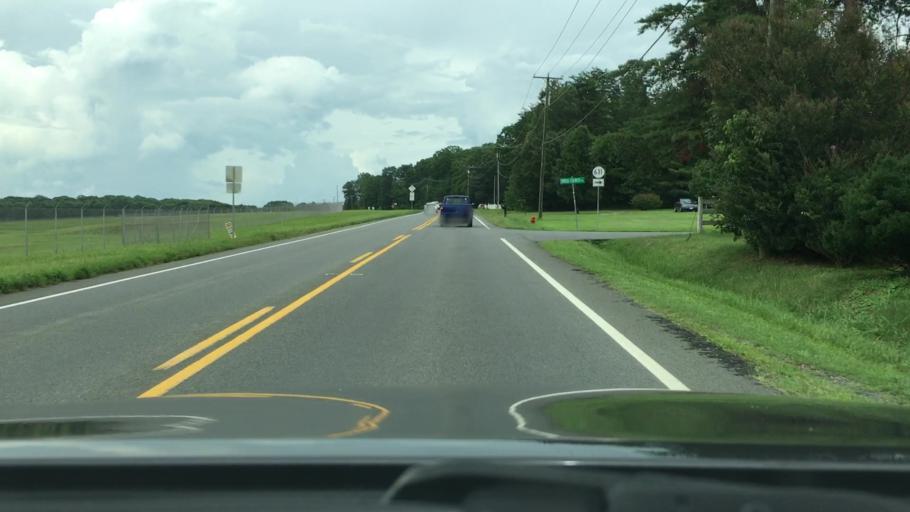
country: US
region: Virginia
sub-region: Orange County
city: Orange
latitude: 38.2466
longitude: -78.0423
